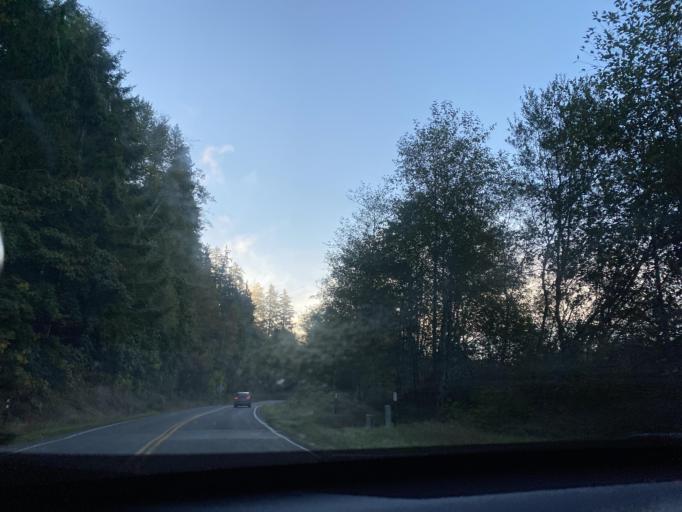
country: US
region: Washington
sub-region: Clallam County
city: Forks
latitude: 47.8198
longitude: -124.1779
